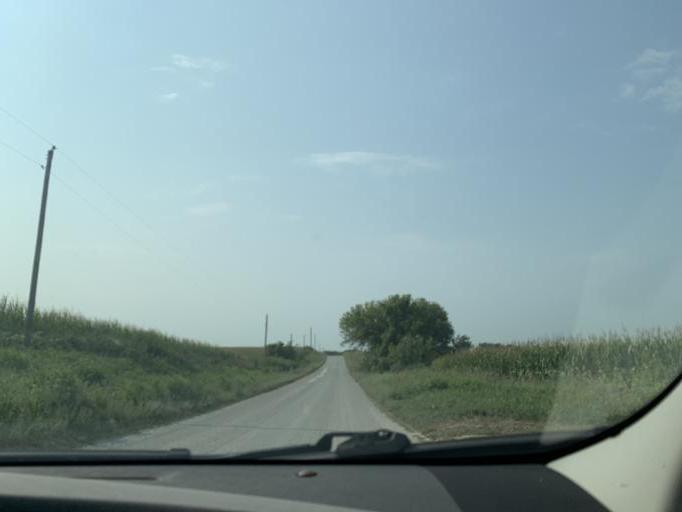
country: US
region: Illinois
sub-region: Whiteside County
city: Sterling
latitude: 41.8299
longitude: -89.7471
